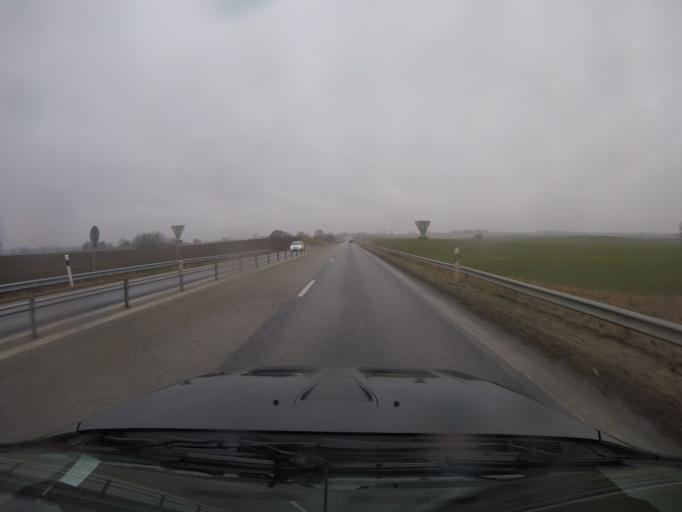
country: SE
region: Skane
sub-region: Svedala Kommun
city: Svedala
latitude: 55.4555
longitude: 13.1895
